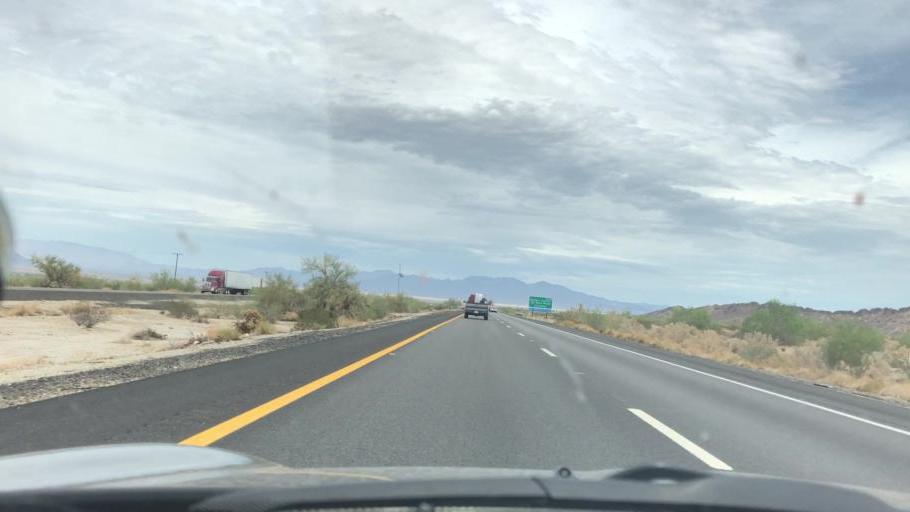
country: US
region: California
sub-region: Imperial County
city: Niland
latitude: 33.7064
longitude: -115.4323
